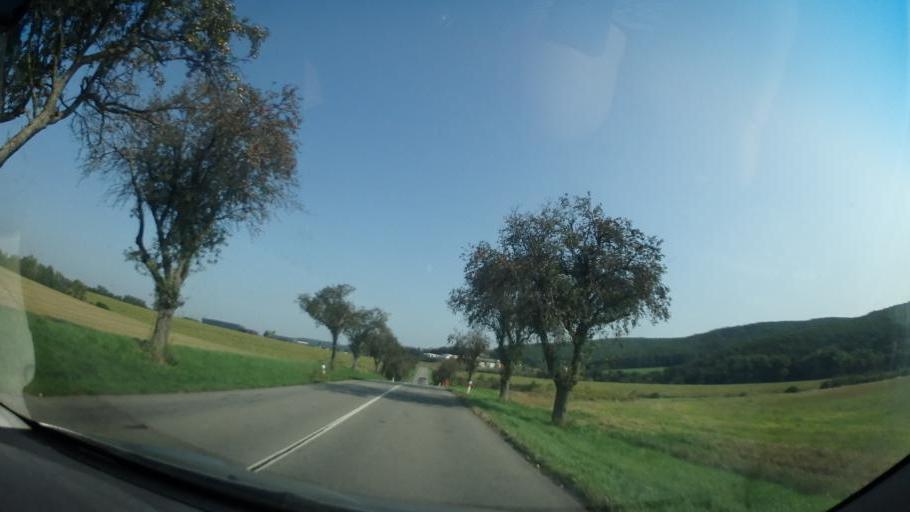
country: CZ
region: South Moravian
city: Kurim
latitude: 49.2560
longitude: 16.5255
